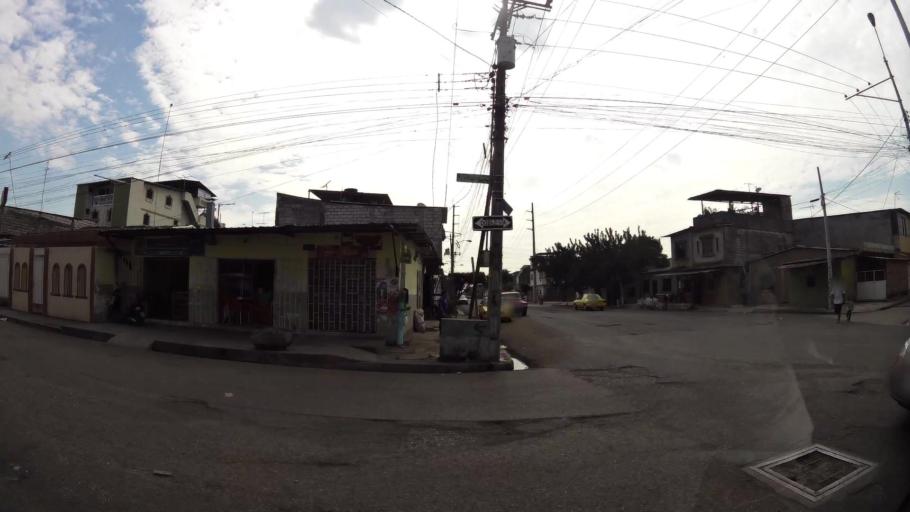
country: EC
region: Guayas
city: Guayaquil
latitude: -2.2512
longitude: -79.8808
